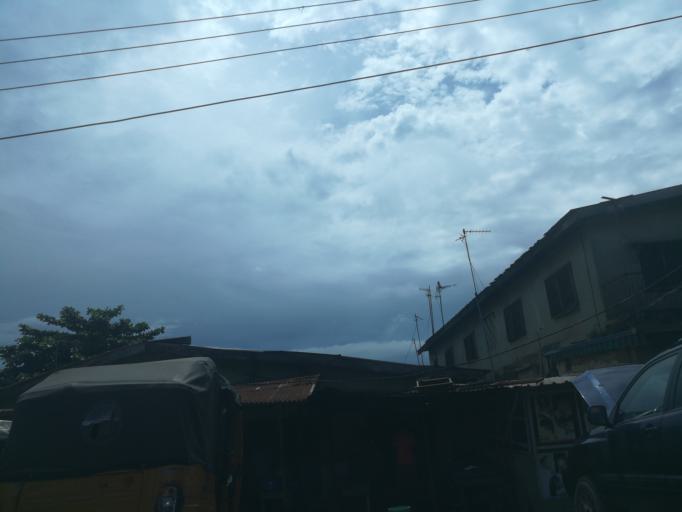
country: NG
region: Lagos
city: Agege
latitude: 6.6171
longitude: 3.3323
